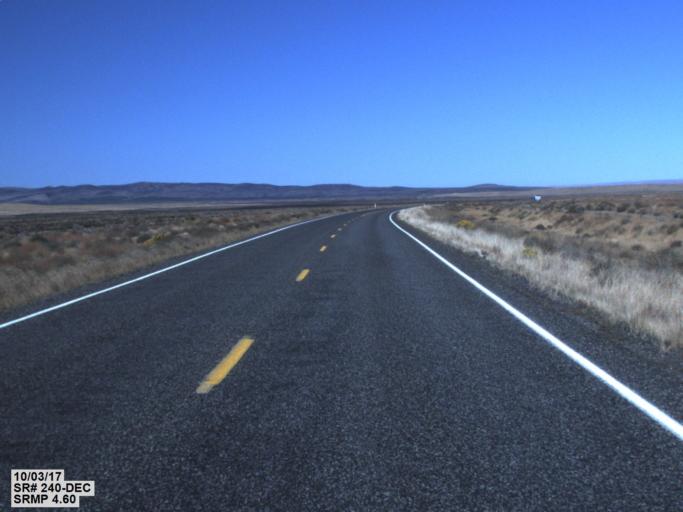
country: US
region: Washington
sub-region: Grant County
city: Desert Aire
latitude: 46.5239
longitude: -119.6766
